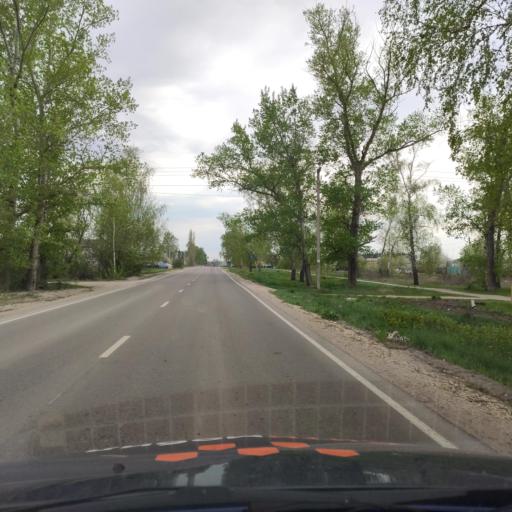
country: RU
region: Voronezj
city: Podgornoye
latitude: 51.8806
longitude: 39.1729
